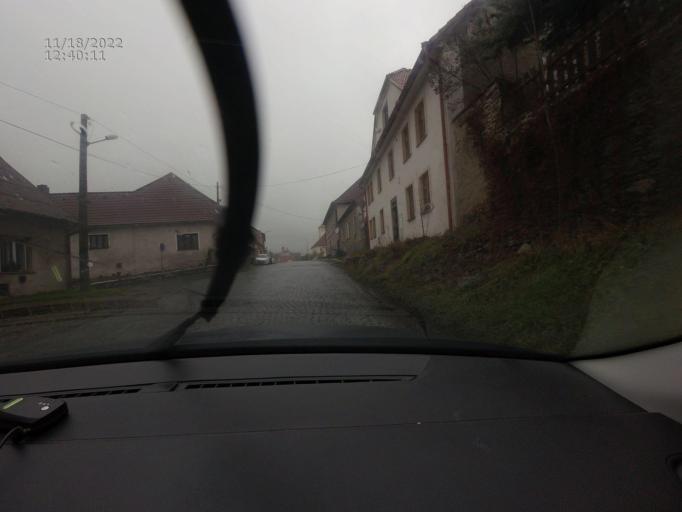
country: CZ
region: Plzensky
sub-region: Okres Klatovy
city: Planice
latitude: 49.3887
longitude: 13.4769
